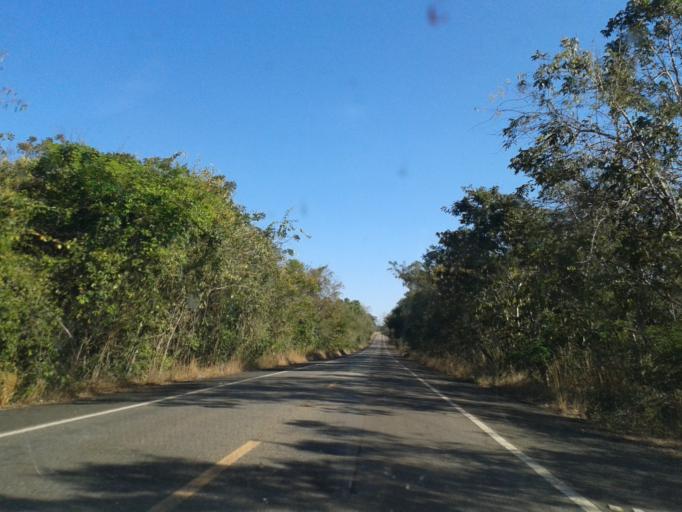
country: BR
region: Goias
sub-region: Mozarlandia
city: Mozarlandia
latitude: -15.0351
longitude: -50.6029
